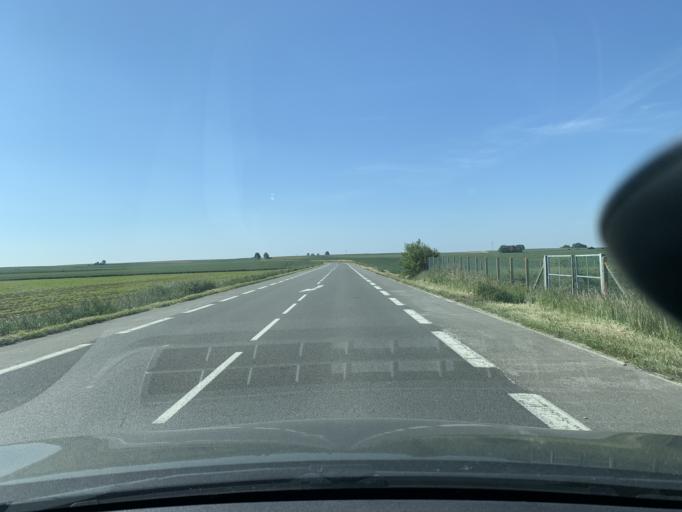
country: FR
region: Nord-Pas-de-Calais
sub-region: Departement du Nord
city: Rumilly-en-Cambresis
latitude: 50.1360
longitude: 3.2465
